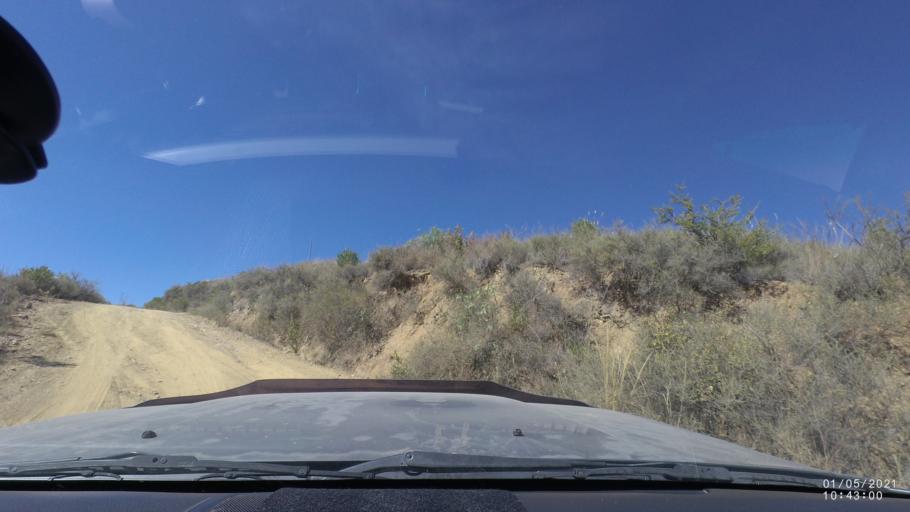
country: BO
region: Cochabamba
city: Capinota
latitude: -17.6142
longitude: -66.1756
